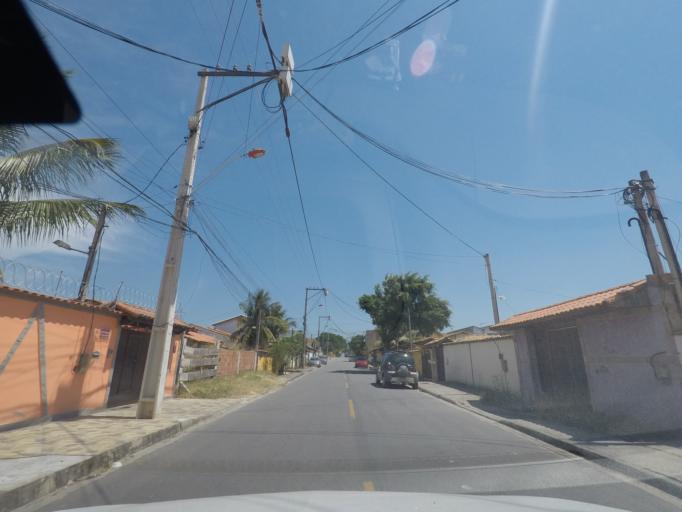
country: BR
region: Rio de Janeiro
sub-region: Marica
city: Marica
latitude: -22.9634
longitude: -42.9567
